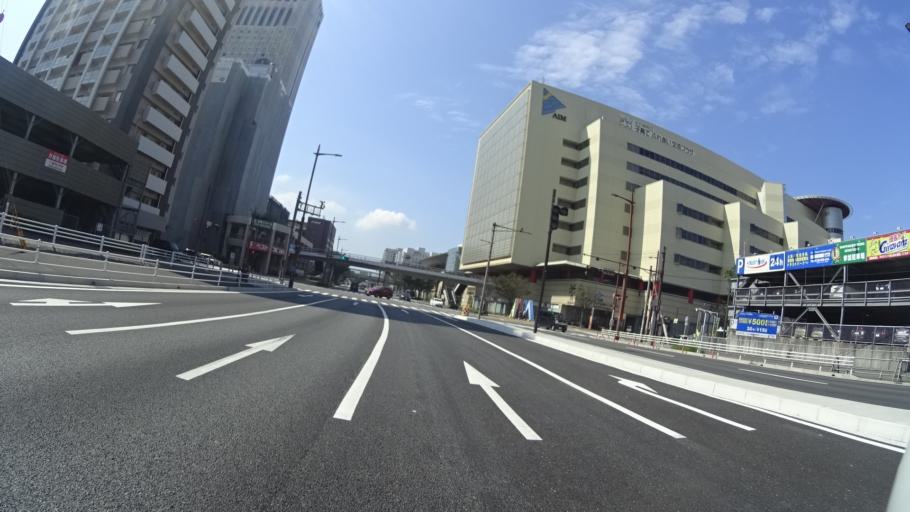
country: JP
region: Fukuoka
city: Kitakyushu
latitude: 33.8881
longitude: 130.8870
